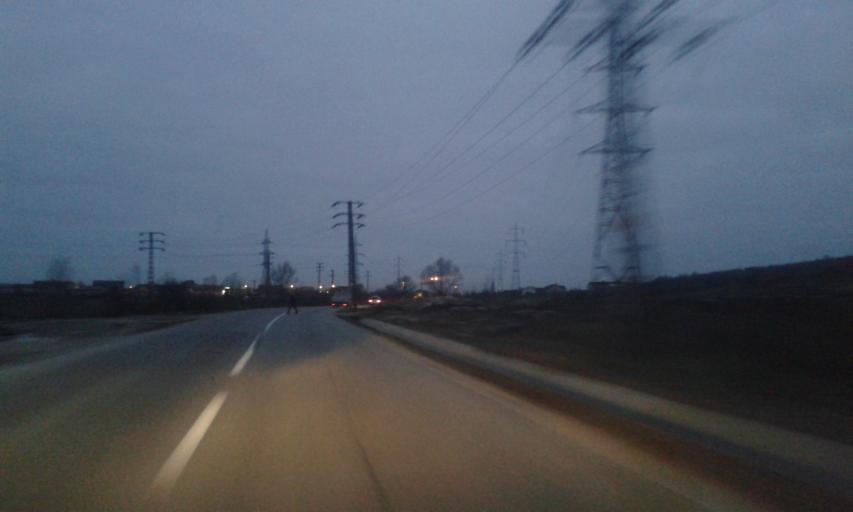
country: RO
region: Gorj
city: Targu Jiu
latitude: 45.0557
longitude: 23.2648
